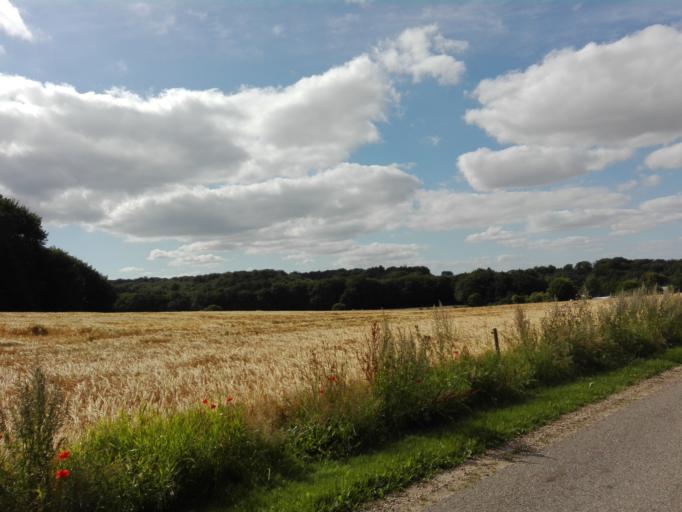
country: DK
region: Central Jutland
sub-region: Skanderborg Kommune
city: Stilling
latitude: 56.1037
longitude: 9.9896
